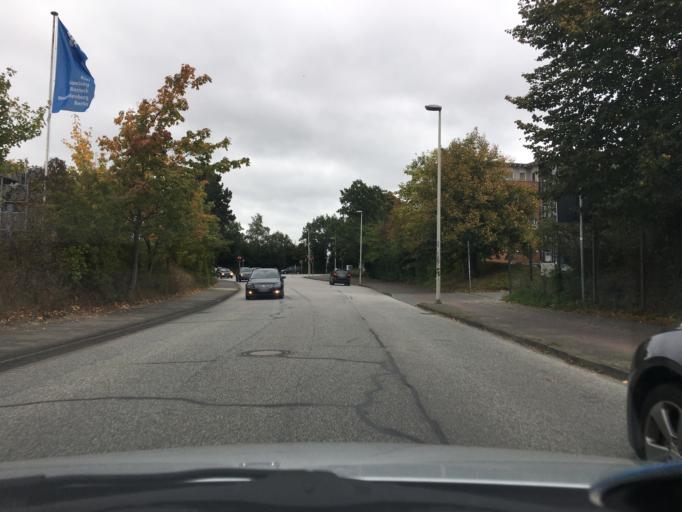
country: DE
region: Schleswig-Holstein
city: Kronshagen
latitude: 54.3386
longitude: 10.1029
